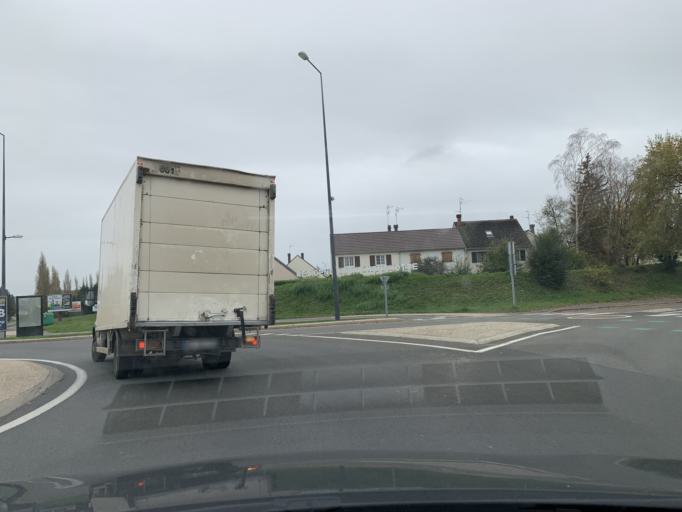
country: FR
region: Nord-Pas-de-Calais
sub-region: Departement du Nord
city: Neuville-Saint-Remy
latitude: 50.1949
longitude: 3.2092
